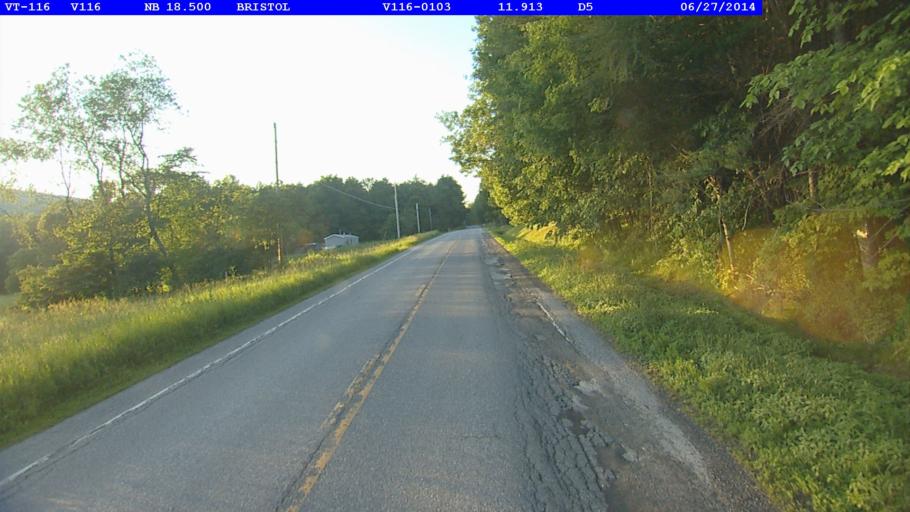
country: US
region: Vermont
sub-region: Addison County
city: Bristol
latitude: 44.1807
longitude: -73.0572
